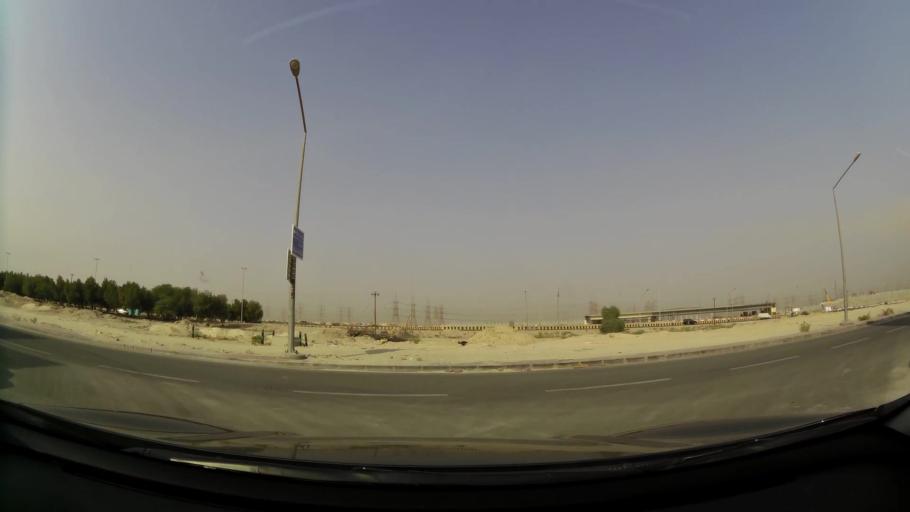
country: KW
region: Al Asimah
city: Ar Rabiyah
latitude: 29.3339
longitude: 47.8005
